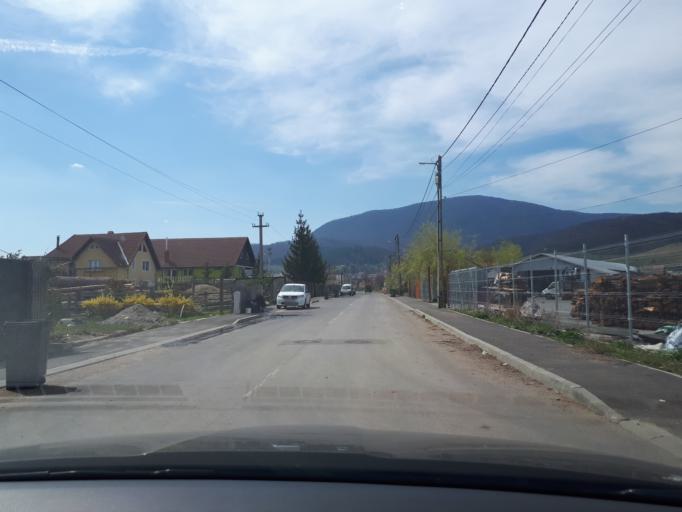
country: RO
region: Brasov
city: Codlea
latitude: 45.7043
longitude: 25.4617
